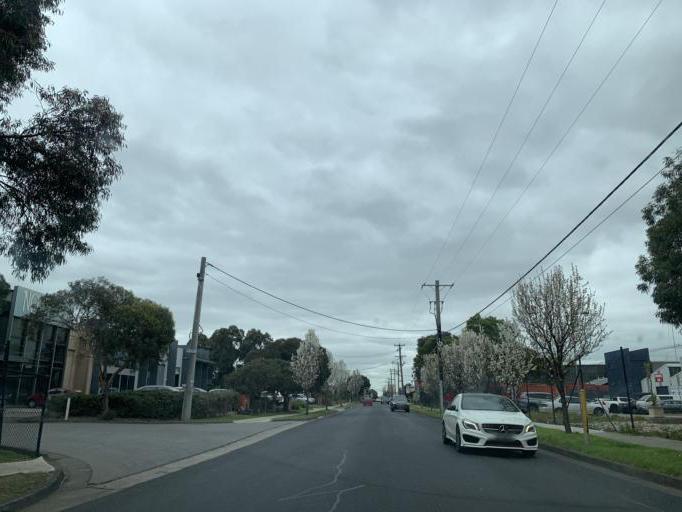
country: AU
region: Victoria
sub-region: Moreland
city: Coburg North
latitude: -37.7286
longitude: 144.9501
